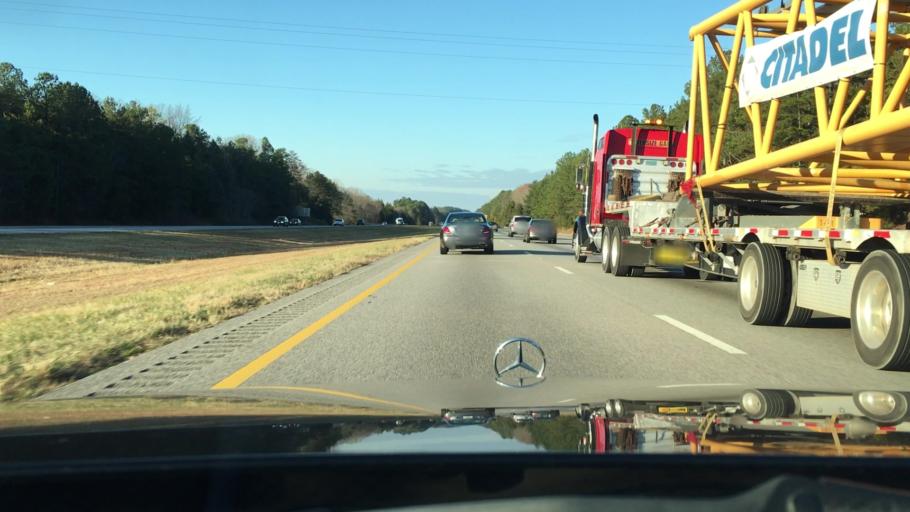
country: US
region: South Carolina
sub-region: Chester County
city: Eureka Mill
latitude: 34.7151
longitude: -81.0315
